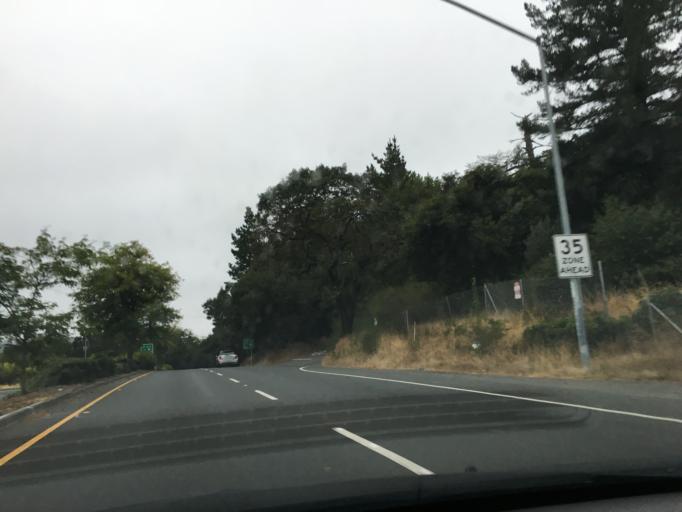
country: US
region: California
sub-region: Sonoma County
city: Santa Rosa
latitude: 38.4533
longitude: -122.6814
